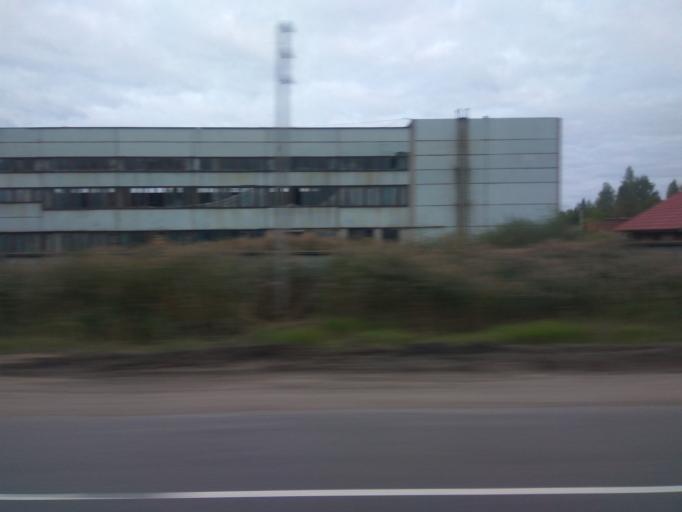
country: RU
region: Moskovskaya
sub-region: Shchelkovskiy Rayon
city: Grebnevo
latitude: 55.9662
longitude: 38.0827
